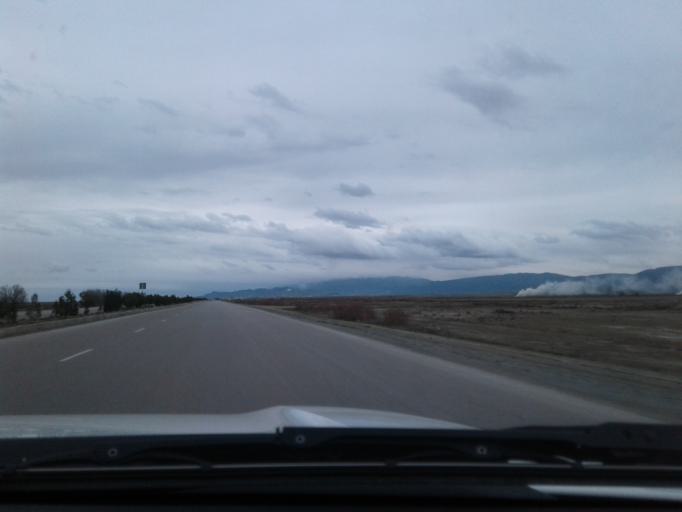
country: TM
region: Ahal
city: Baharly
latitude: 38.3606
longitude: 57.5323
